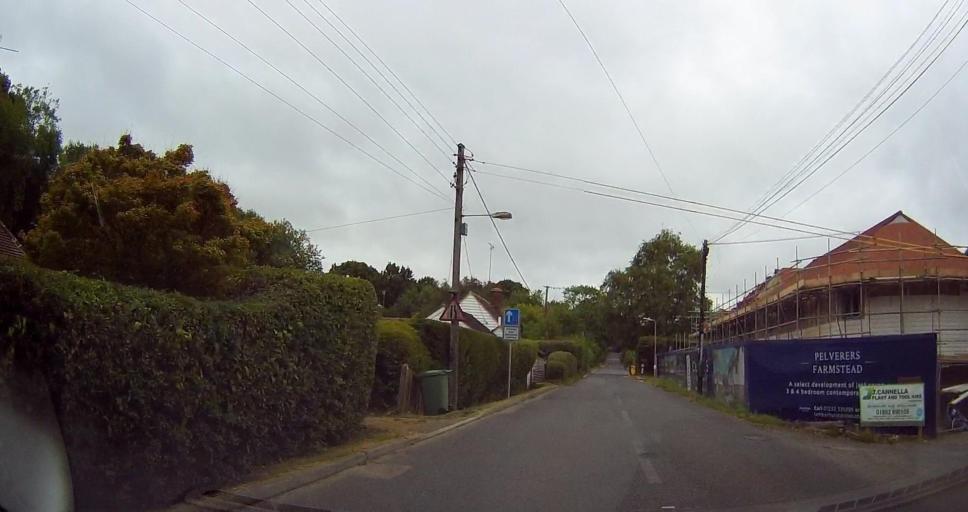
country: GB
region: England
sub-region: East Sussex
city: Wadhurst
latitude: 51.0905
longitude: 0.3860
